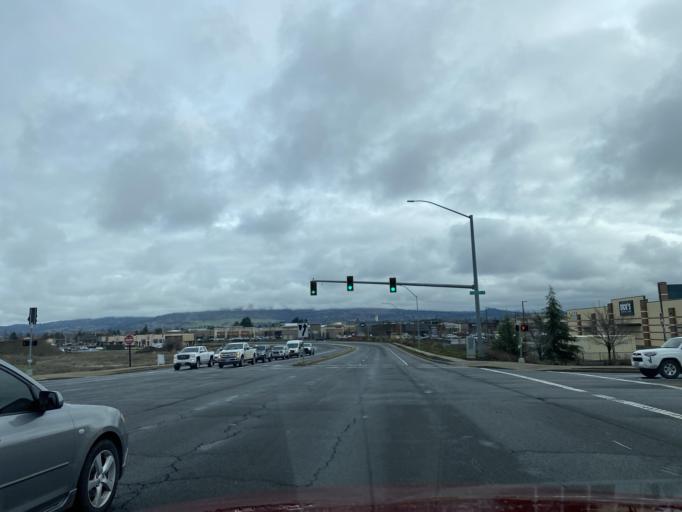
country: US
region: Oregon
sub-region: Jackson County
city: Medford
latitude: 42.3430
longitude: -122.8867
